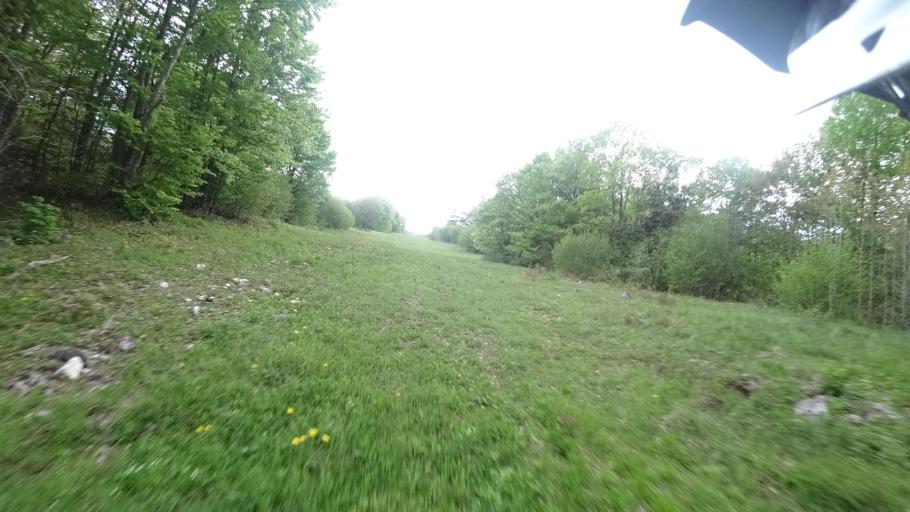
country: HR
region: Karlovacka
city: Plaski
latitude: 44.9050
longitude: 15.4155
